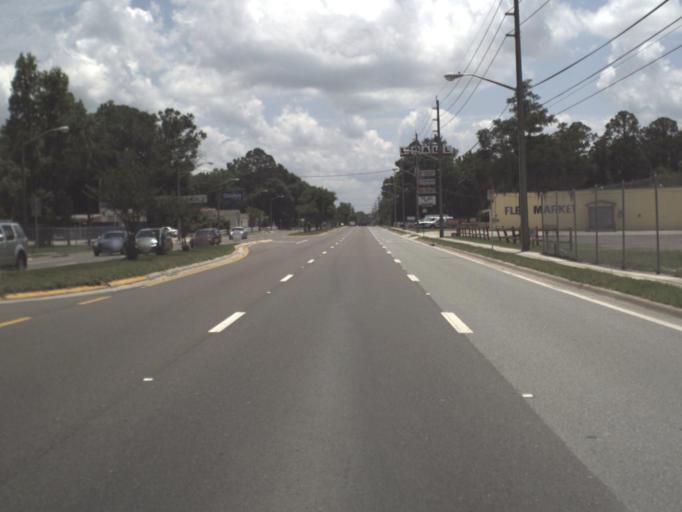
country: US
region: Florida
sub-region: Clay County
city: Bellair-Meadowbrook Terrace
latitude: 30.2416
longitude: -81.7421
